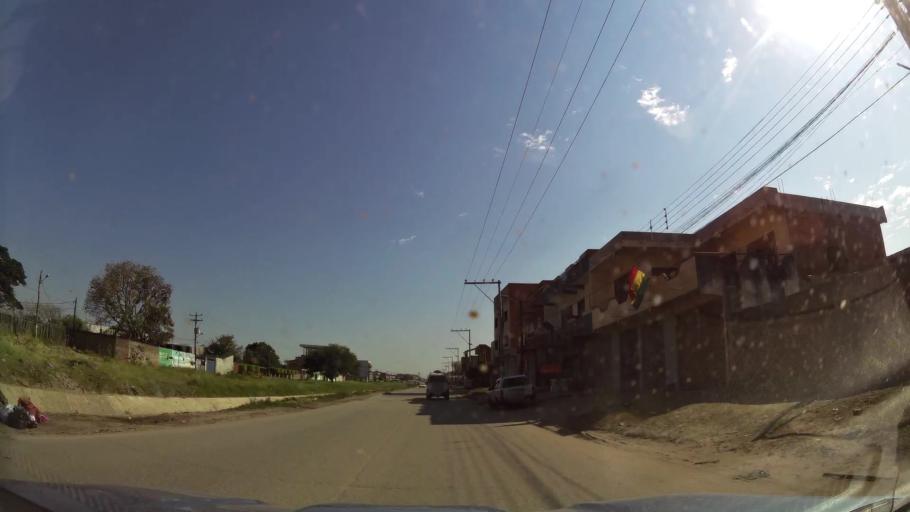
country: BO
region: Santa Cruz
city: Santa Cruz de la Sierra
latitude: -17.8205
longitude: -63.1231
